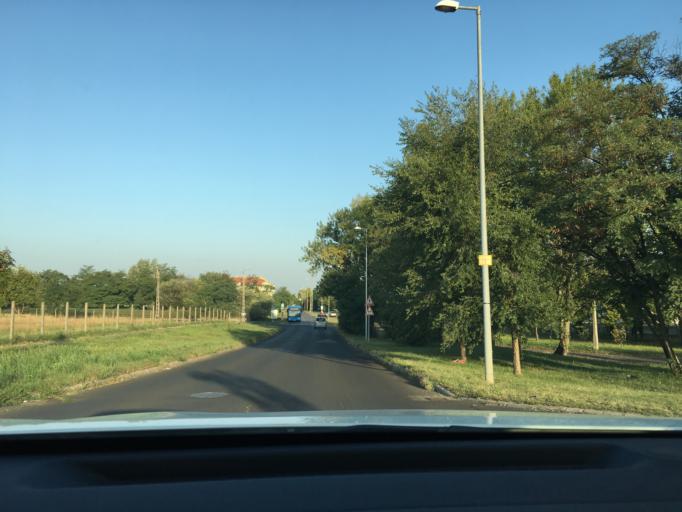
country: HU
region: Budapest
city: Budapest XVII. keruelet
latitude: 47.4785
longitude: 19.2389
